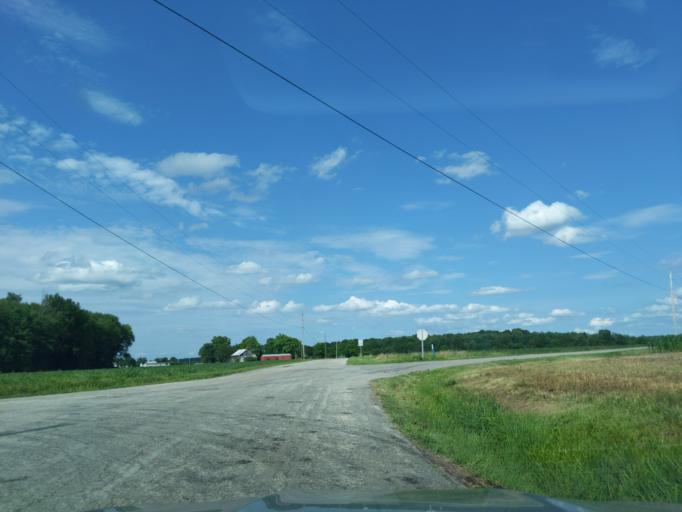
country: US
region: Indiana
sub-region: Ripley County
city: Sunman
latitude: 39.3098
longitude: -85.0755
